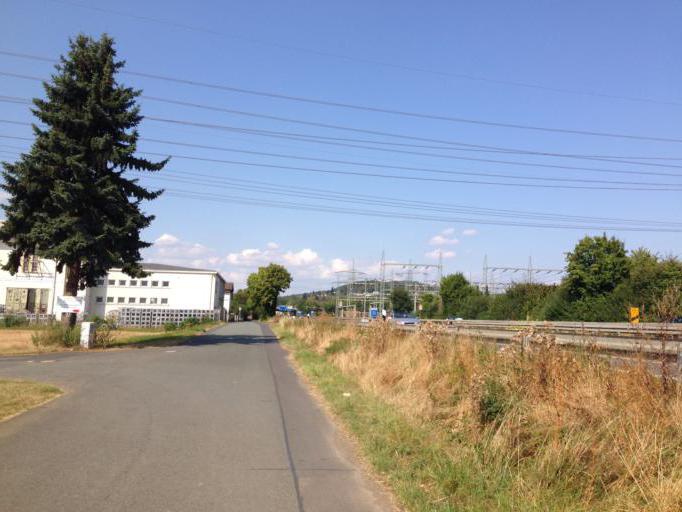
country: DE
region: Hesse
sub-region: Regierungsbezirk Giessen
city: Giessen
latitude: 50.6024
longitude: 8.6554
